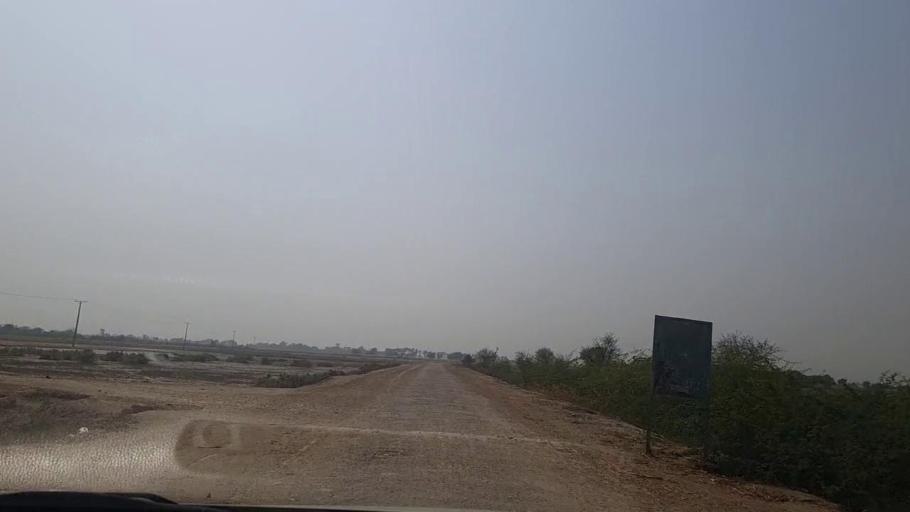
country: PK
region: Sindh
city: Pithoro
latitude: 25.5614
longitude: 69.2540
